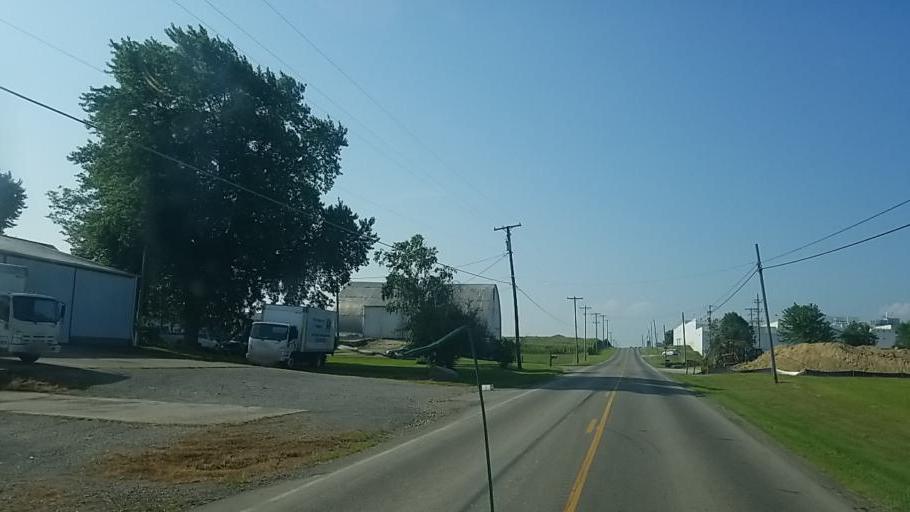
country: US
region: Ohio
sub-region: Wayne County
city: Dalton
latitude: 40.7305
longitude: -81.7451
